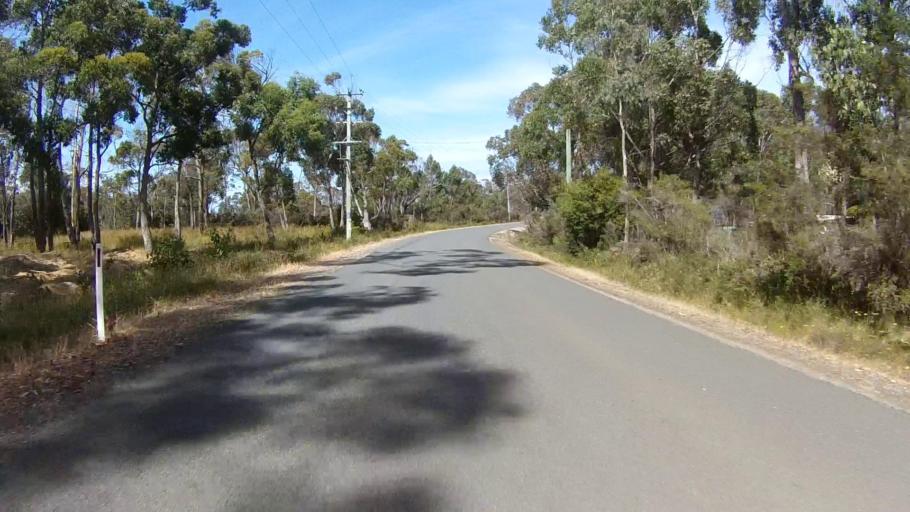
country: AU
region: Tasmania
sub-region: Huon Valley
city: Cygnet
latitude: -43.2405
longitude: 147.1236
